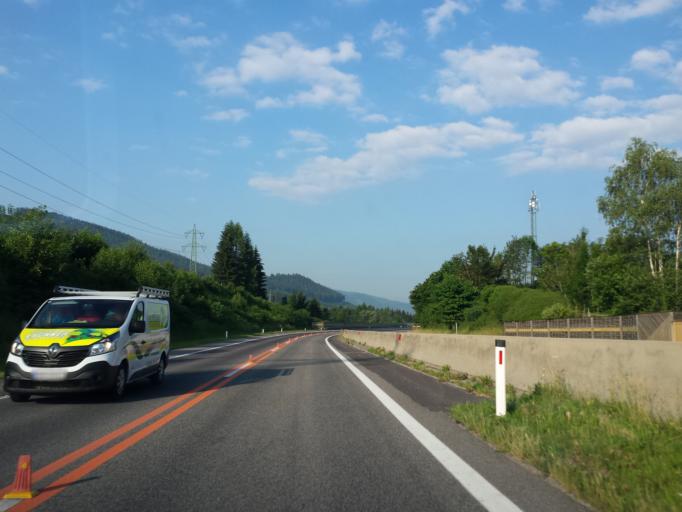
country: AT
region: Styria
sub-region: Politischer Bezirk Bruck-Muerzzuschlag
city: Langenwang
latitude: 47.5703
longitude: 15.6390
